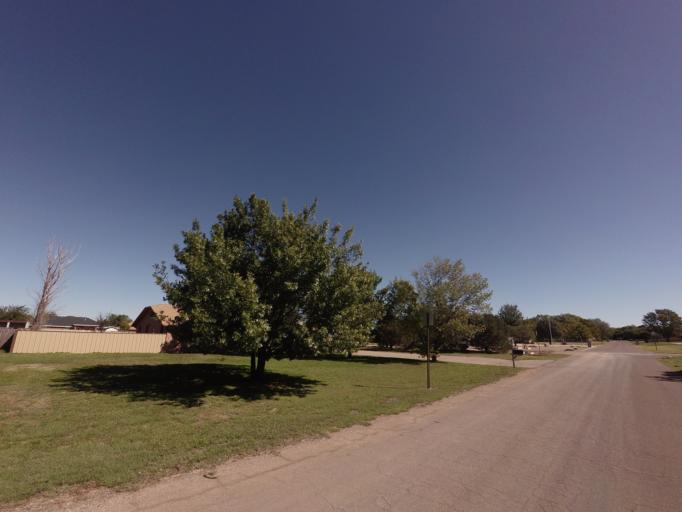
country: US
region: New Mexico
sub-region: Curry County
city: Clovis
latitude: 34.4276
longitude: -103.1727
